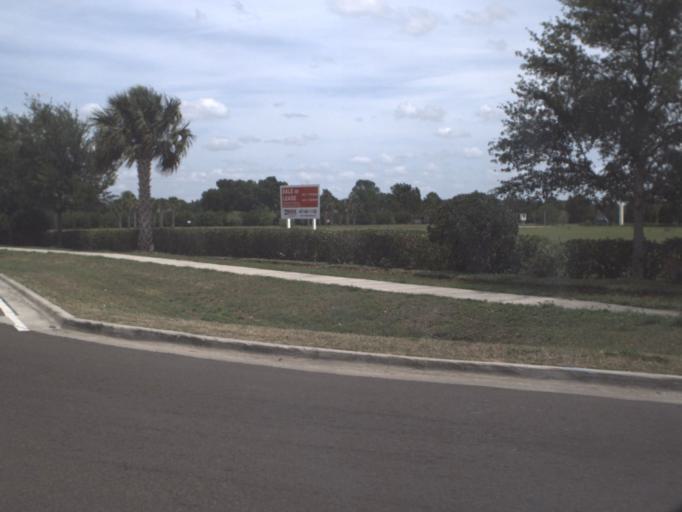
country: US
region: Florida
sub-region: Lake County
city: Mount Dora
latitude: 28.8259
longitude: -81.6438
